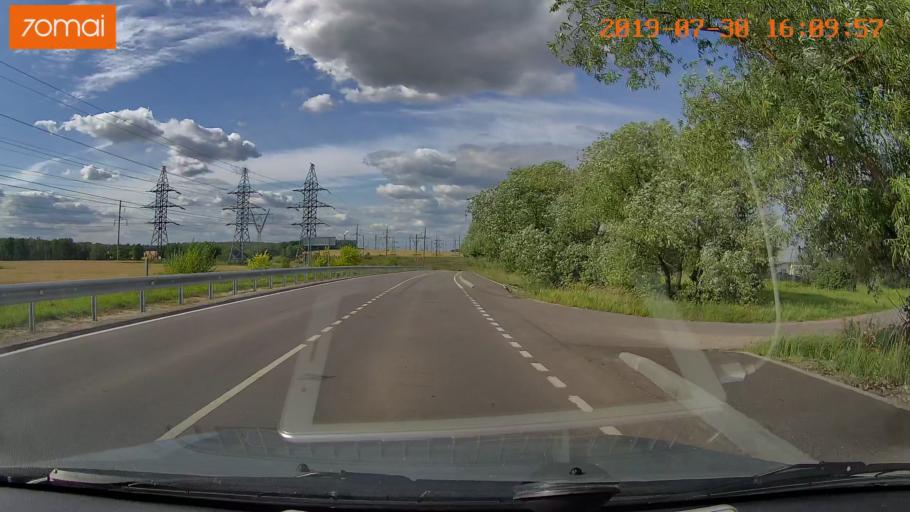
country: RU
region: Moskovskaya
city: Peski
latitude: 55.2578
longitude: 38.7157
